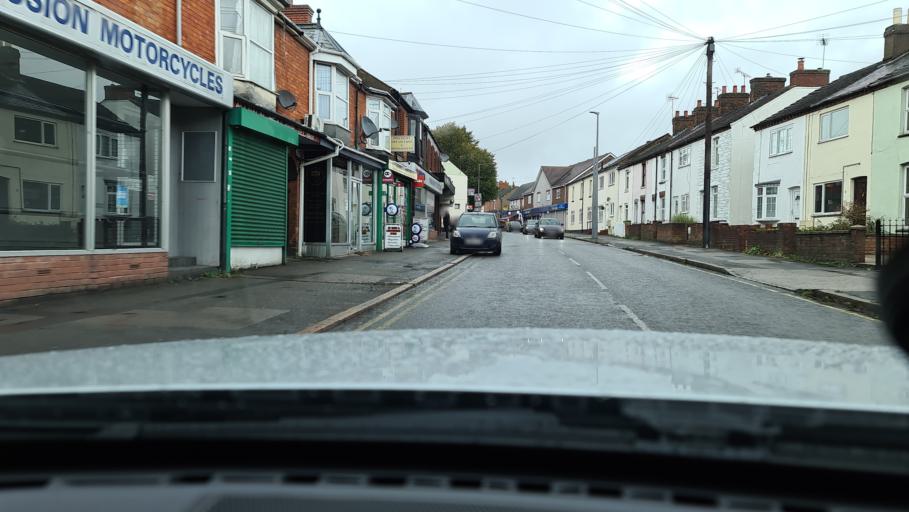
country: GB
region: England
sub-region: Milton Keynes
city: Water Eaton
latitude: 51.9964
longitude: -0.7207
